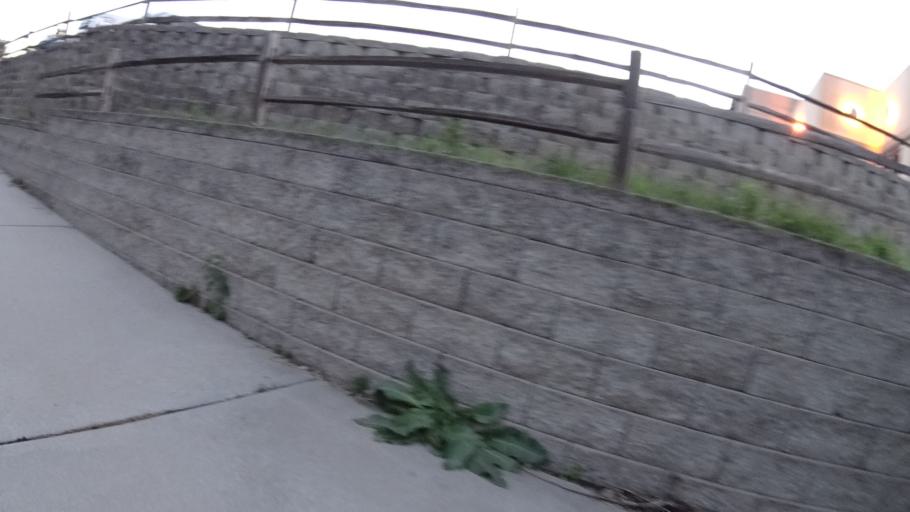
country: US
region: Nebraska
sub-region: Sarpy County
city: Offutt Air Force Base
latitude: 41.1415
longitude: -95.9731
